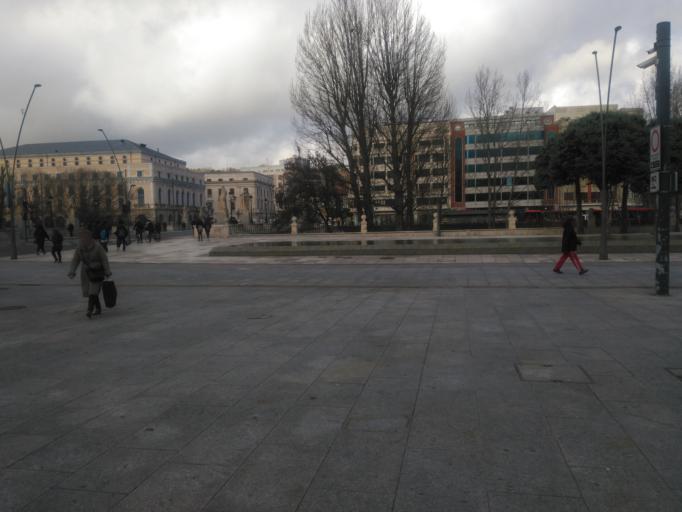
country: ES
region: Castille and Leon
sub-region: Provincia de Burgos
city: Burgos
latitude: 42.3396
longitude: -3.6986
